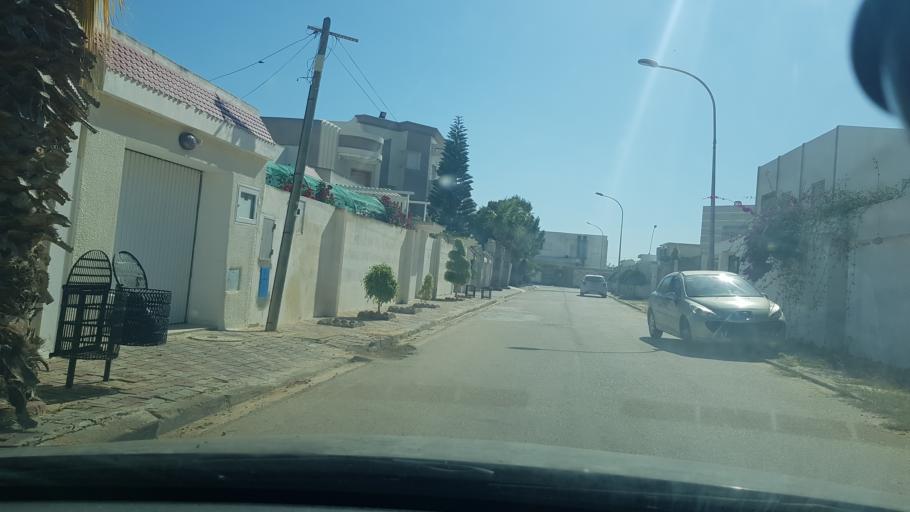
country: TN
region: Safaqis
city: Al Qarmadah
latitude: 34.8246
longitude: 10.7592
